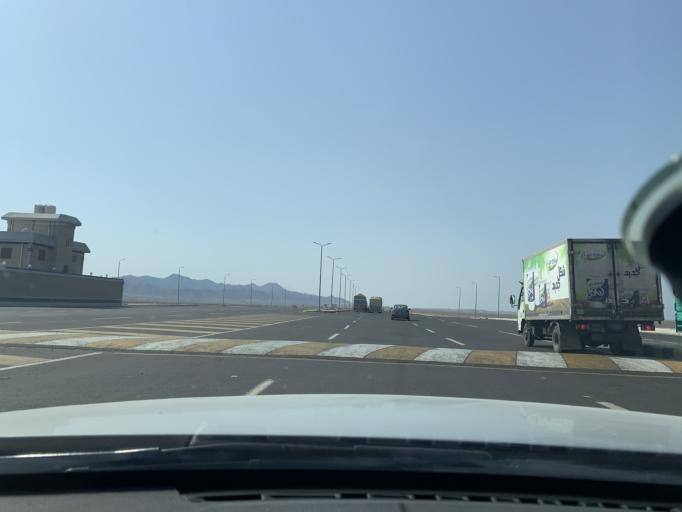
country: EG
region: Red Sea
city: El Gouna
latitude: 27.4309
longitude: 33.6093
